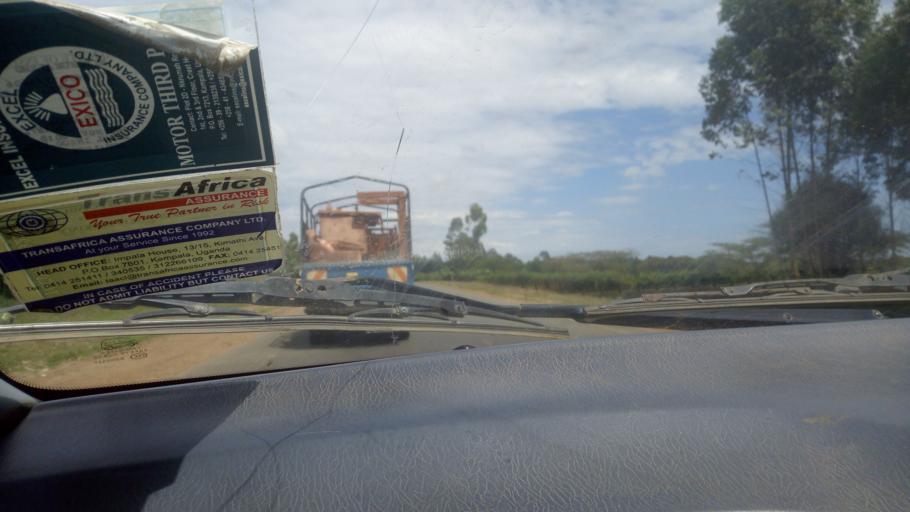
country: UG
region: Western Region
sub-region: Mbarara District
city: Bwizibwera
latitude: -0.4269
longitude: 30.5709
